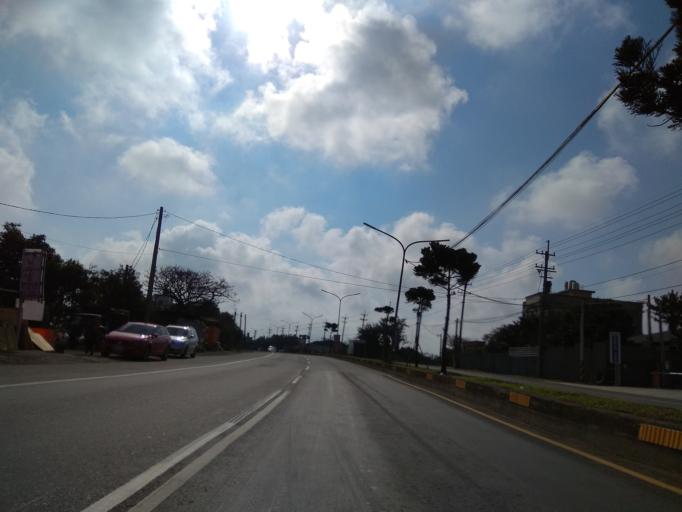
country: TW
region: Taiwan
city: Taoyuan City
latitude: 25.0415
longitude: 121.1046
